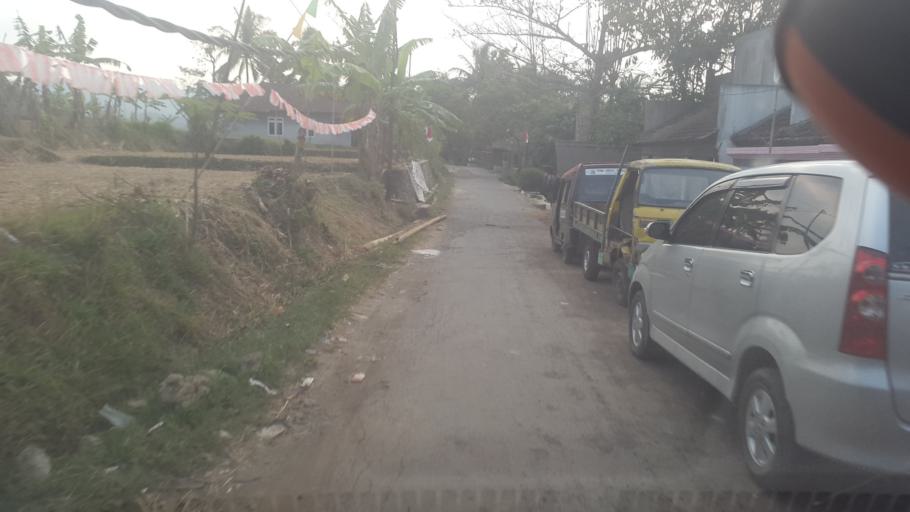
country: ID
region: West Java
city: Sukamaju
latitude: -7.0063
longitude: 106.8964
